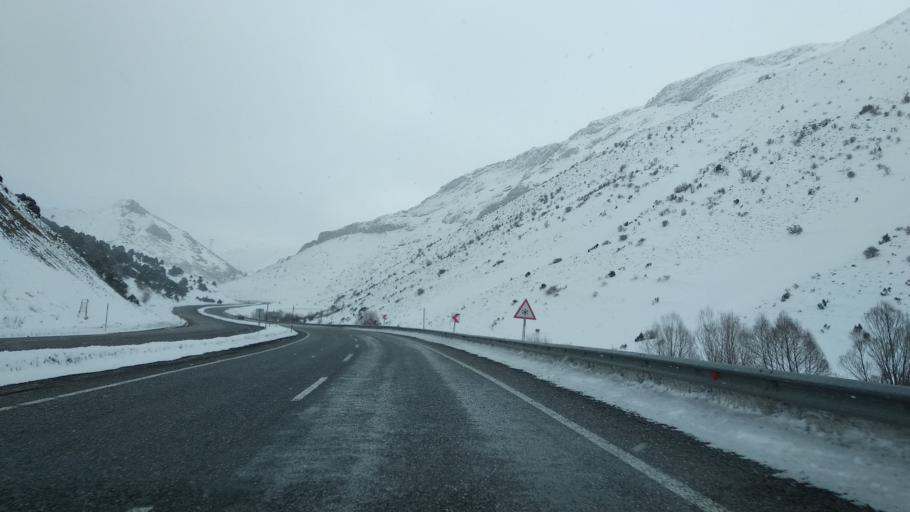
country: TR
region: Kayseri
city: Sariz
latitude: 38.5577
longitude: 36.4440
